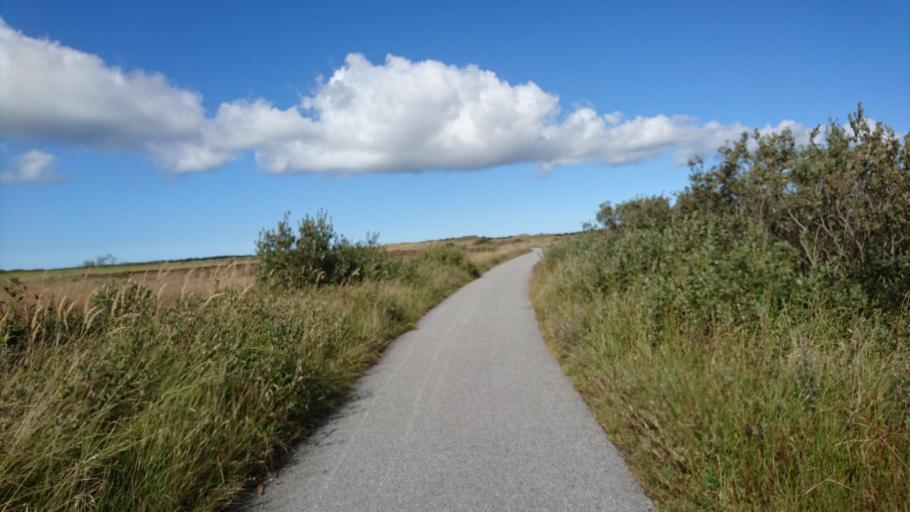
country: DK
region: North Denmark
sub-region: Frederikshavn Kommune
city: Skagen
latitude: 57.6845
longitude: 10.5029
